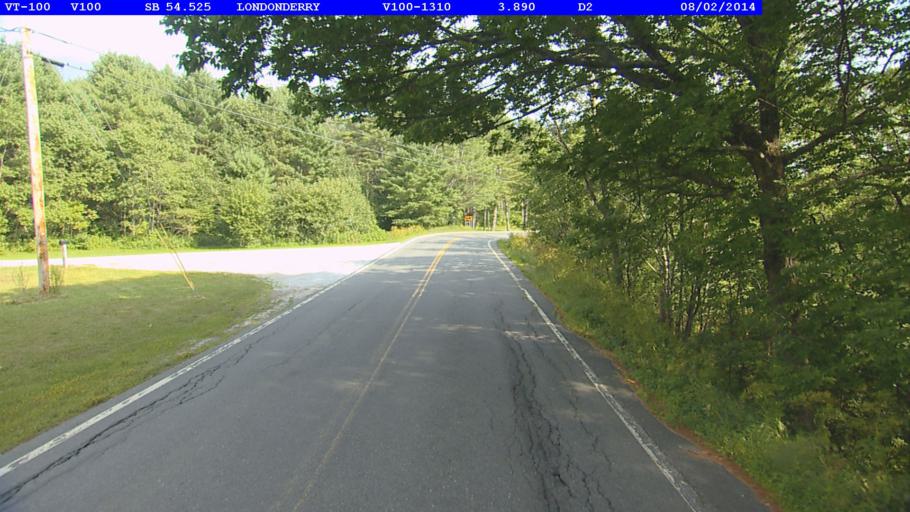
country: US
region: Vermont
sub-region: Windsor County
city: Chester
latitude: 43.2036
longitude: -72.8220
